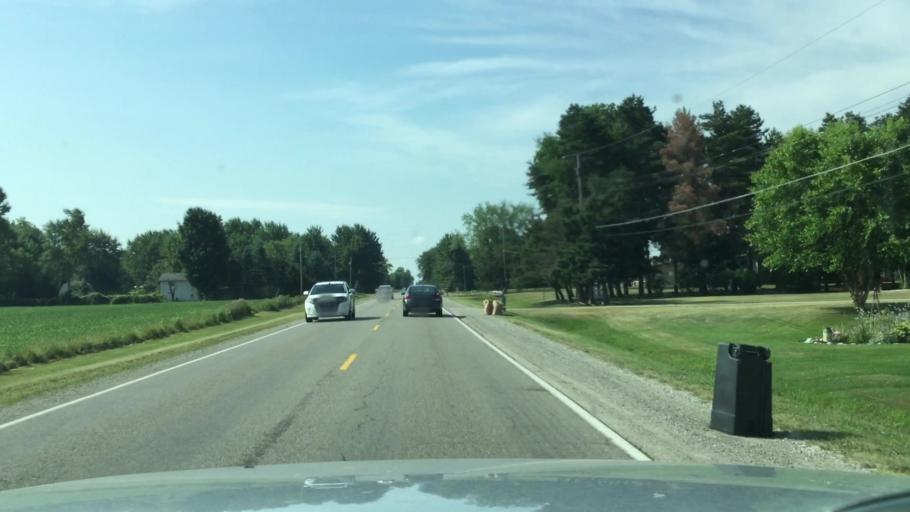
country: US
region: Michigan
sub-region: Genesee County
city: Flushing
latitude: 43.1089
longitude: -83.8137
